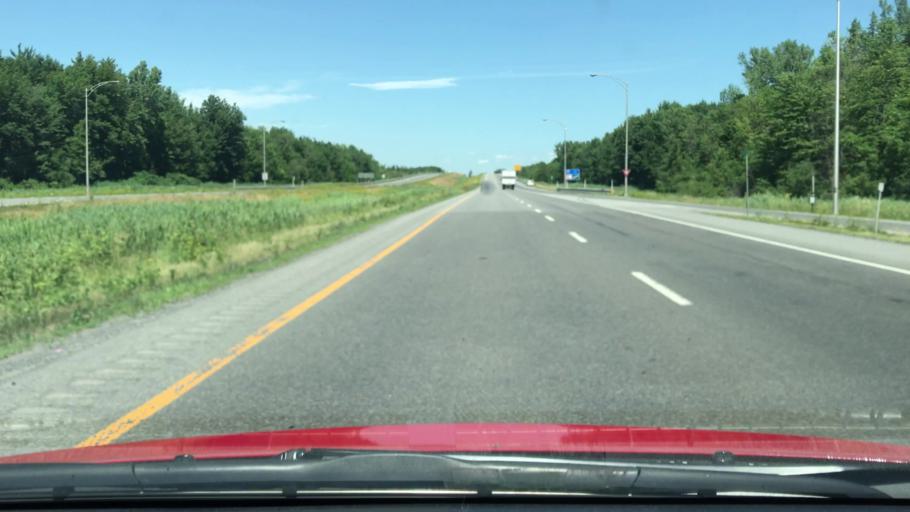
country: CA
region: Quebec
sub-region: Monteregie
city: Saint-Constant
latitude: 45.3802
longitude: -73.6139
